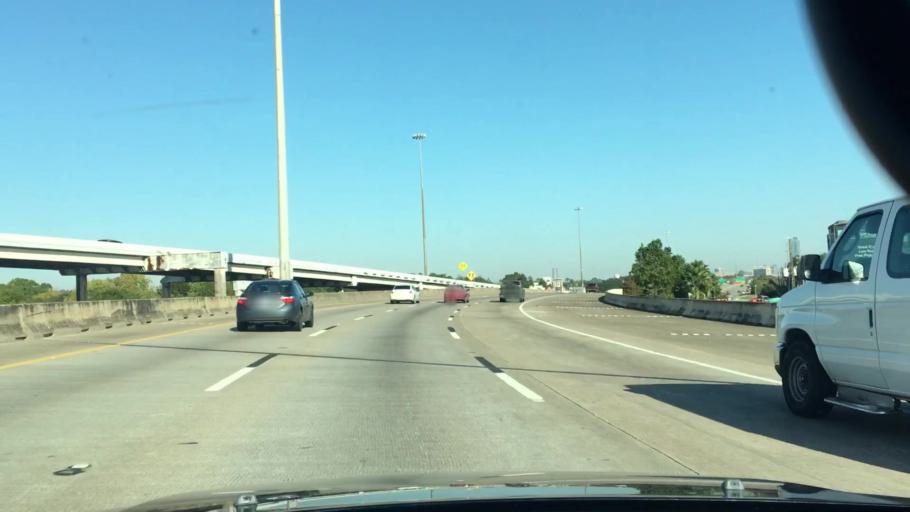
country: US
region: Texas
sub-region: Harris County
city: Bellaire
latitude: 29.6812
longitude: -95.4585
